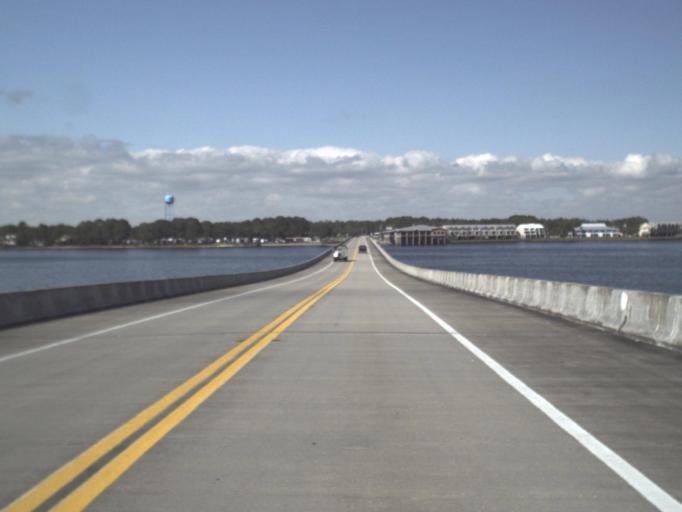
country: US
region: Florida
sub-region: Wakulla County
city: Crawfordville
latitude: 29.9704
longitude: -84.3838
